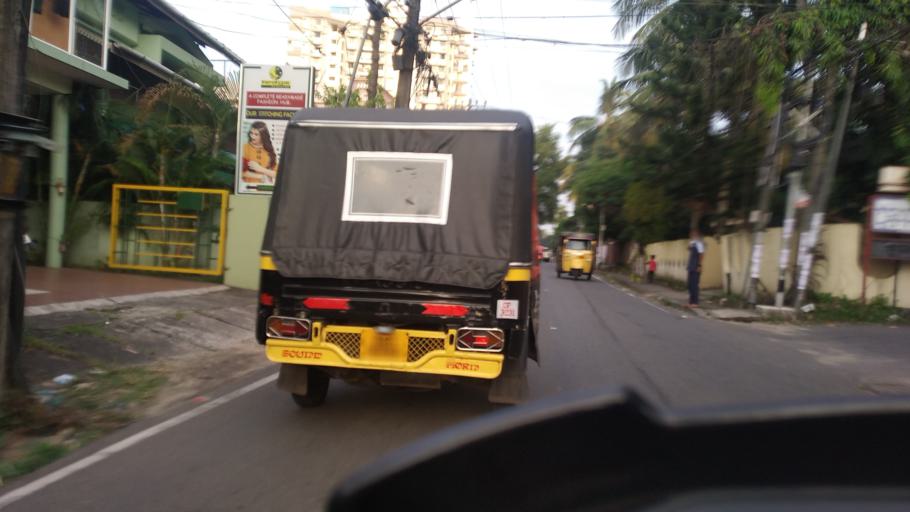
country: IN
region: Kerala
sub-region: Ernakulam
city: Elur
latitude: 10.0198
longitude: 76.2977
